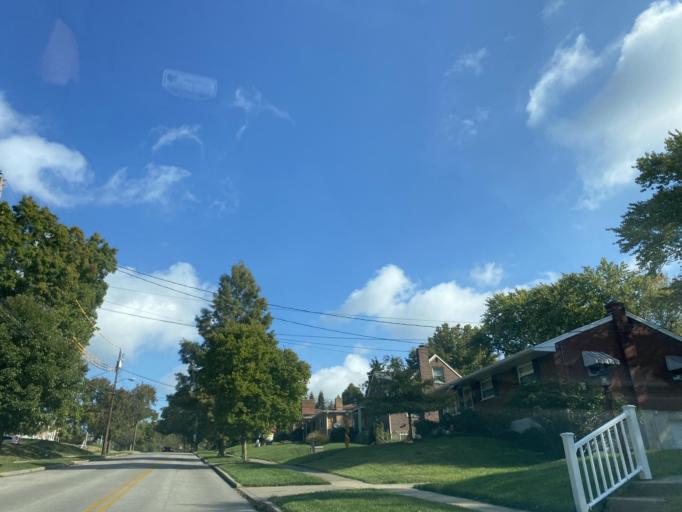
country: US
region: Kentucky
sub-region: Campbell County
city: Fort Thomas
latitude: 39.0945
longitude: -84.4564
